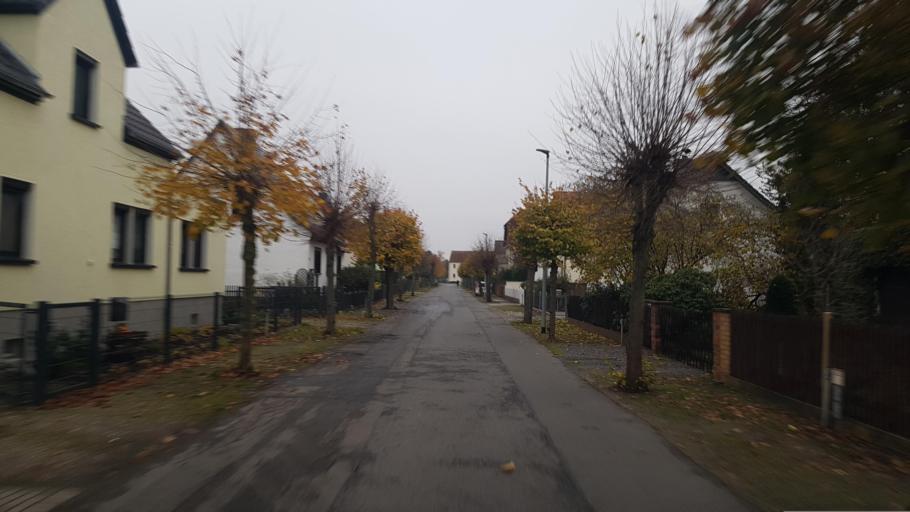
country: DE
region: Brandenburg
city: Ruhland
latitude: 51.4532
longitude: 13.8702
